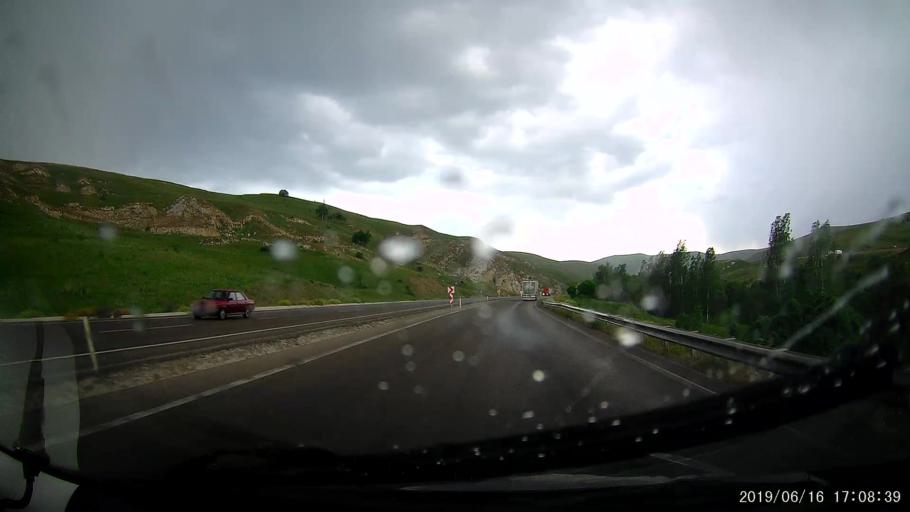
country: TR
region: Erzurum
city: Askale
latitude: 39.9055
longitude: 40.6592
